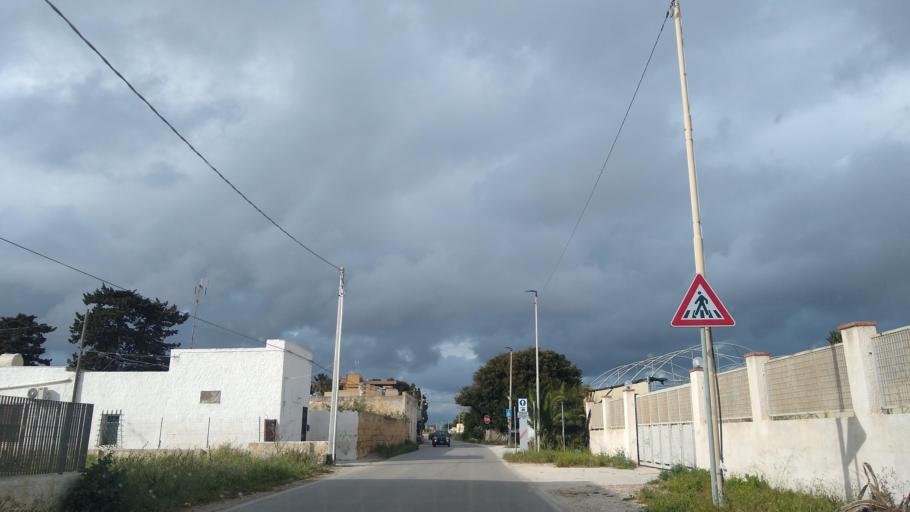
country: IT
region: Sicily
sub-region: Trapani
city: Marsala
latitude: 37.8549
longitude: 12.4865
